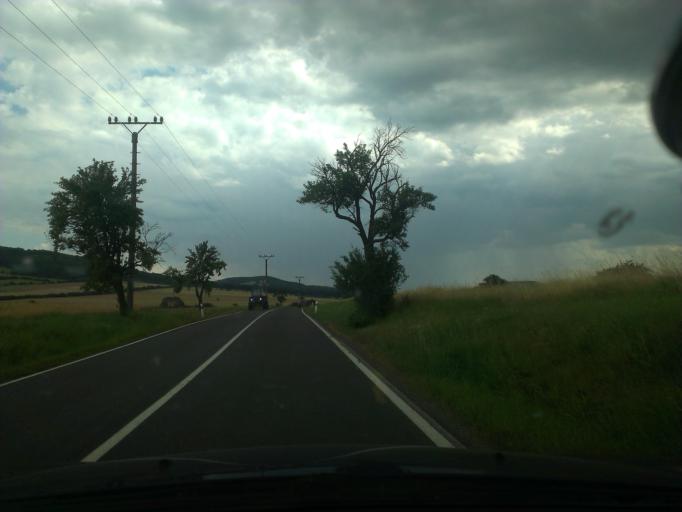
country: CZ
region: South Moravian
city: Velka nad Velickou
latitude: 48.8581
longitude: 17.5226
